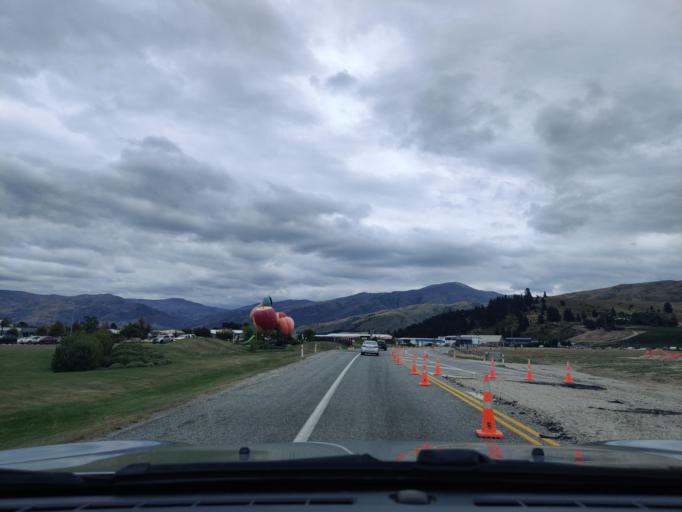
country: NZ
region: Otago
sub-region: Queenstown-Lakes District
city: Wanaka
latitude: -45.0351
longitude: 169.1988
